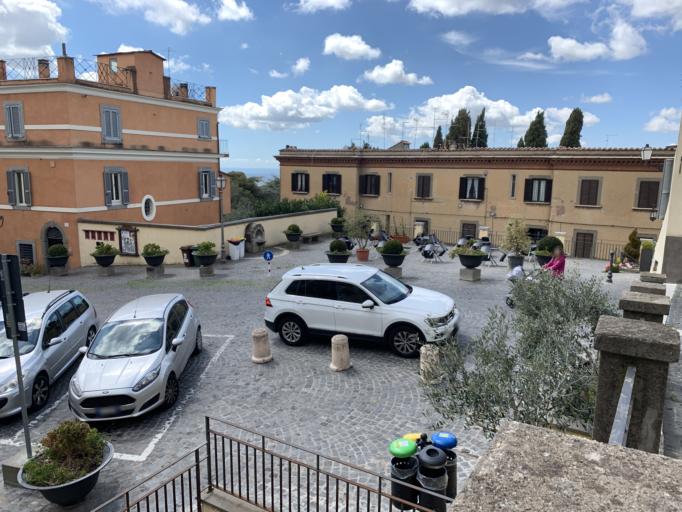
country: IT
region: Latium
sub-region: Citta metropolitana di Roma Capitale
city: Castel Gandolfo
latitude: 41.7448
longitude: 12.6512
